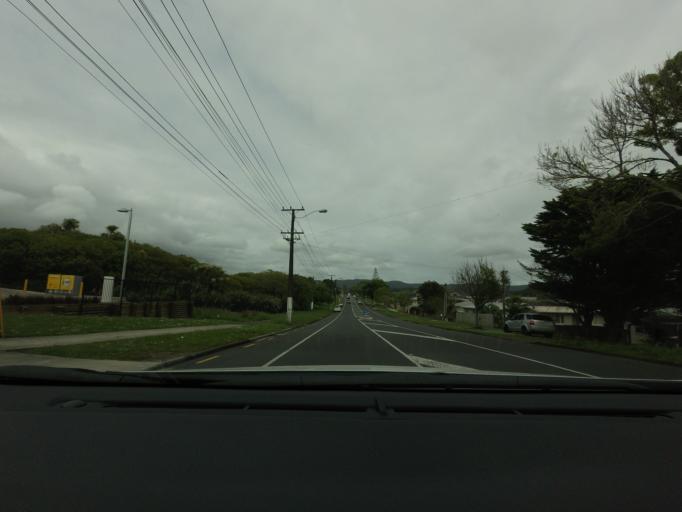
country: NZ
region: Auckland
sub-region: Auckland
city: Waitakere
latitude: -36.8917
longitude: 174.6227
